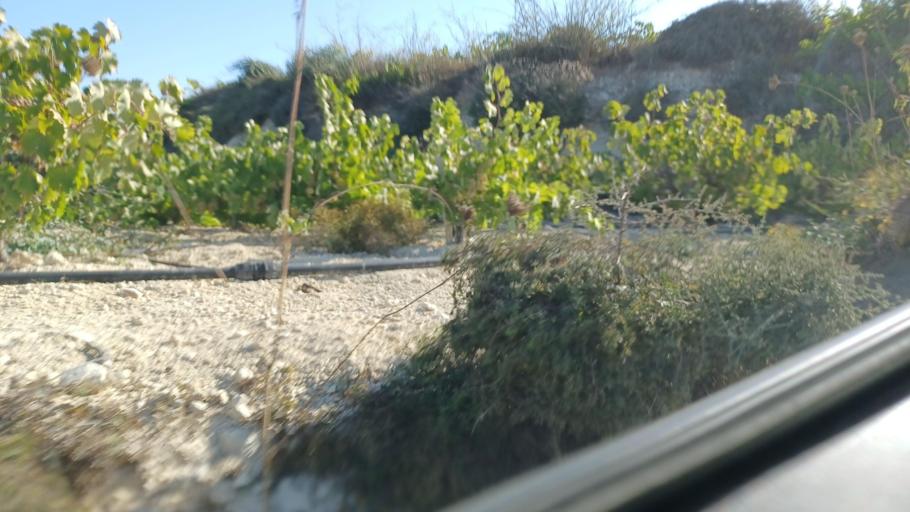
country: CY
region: Pafos
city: Tala
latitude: 34.8687
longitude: 32.4535
